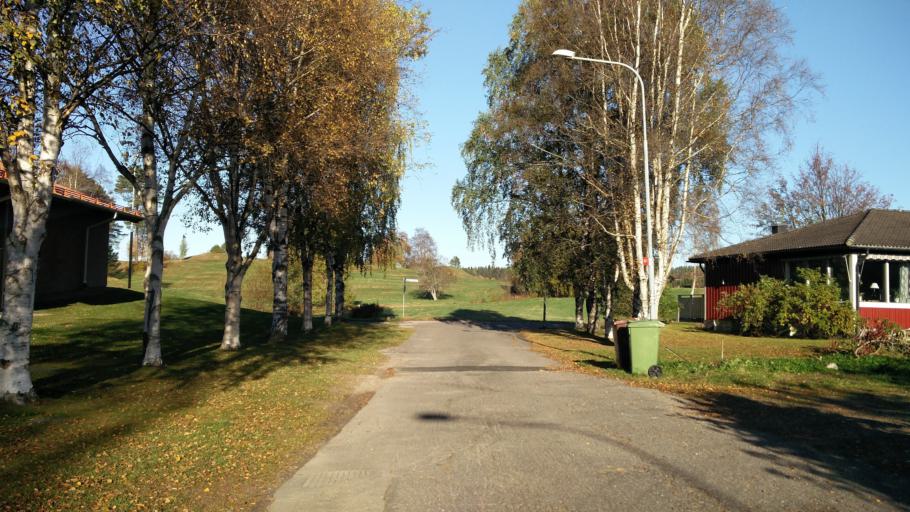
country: SE
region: Vaesternorrland
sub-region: Sundsvalls Kommun
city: Sundsvall
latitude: 62.3997
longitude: 17.2625
